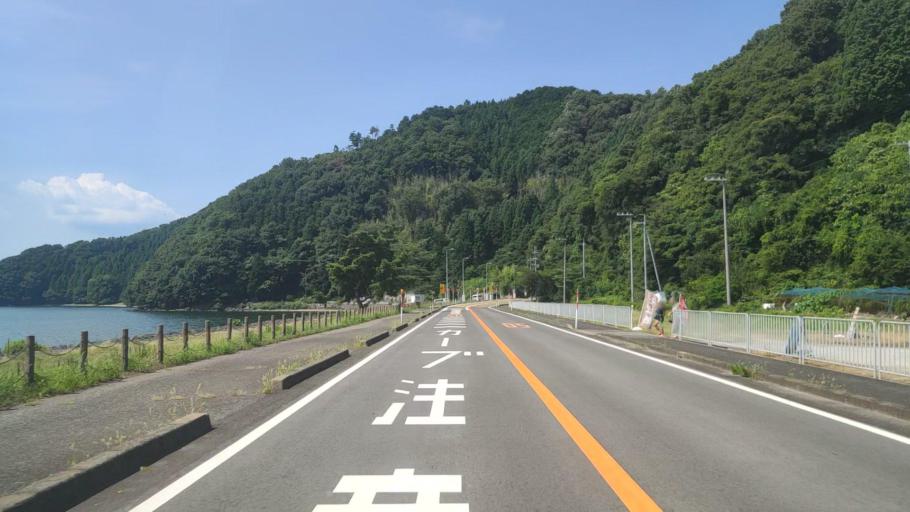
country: JP
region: Shiga Prefecture
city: Nagahama
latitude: 35.4571
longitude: 136.1986
